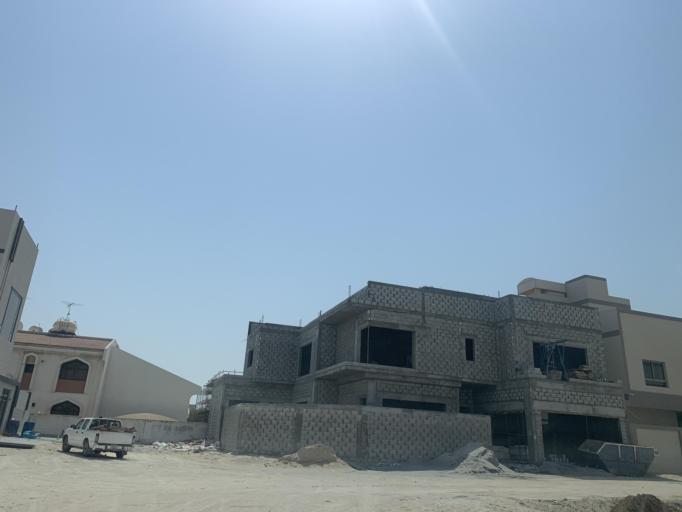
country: BH
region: Manama
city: Jidd Hafs
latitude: 26.2008
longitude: 50.5261
